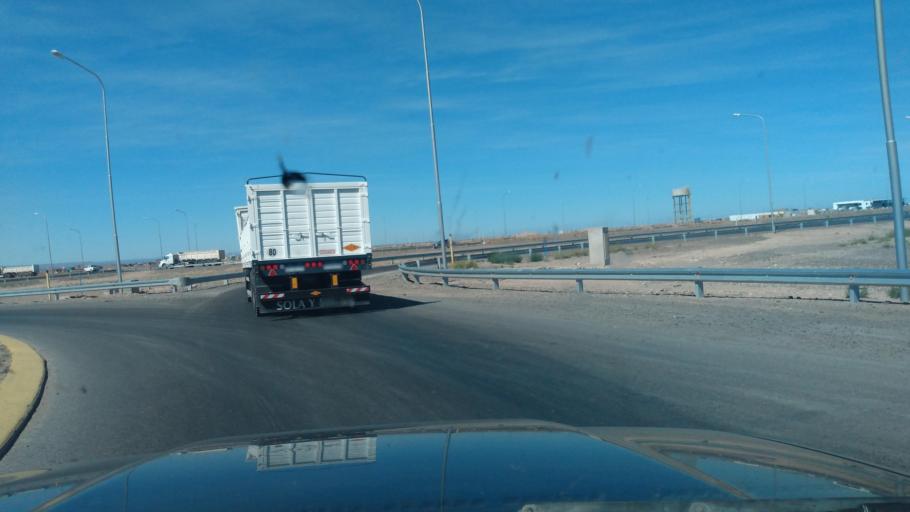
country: AR
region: Neuquen
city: Neuquen
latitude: -38.9109
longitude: -68.1211
